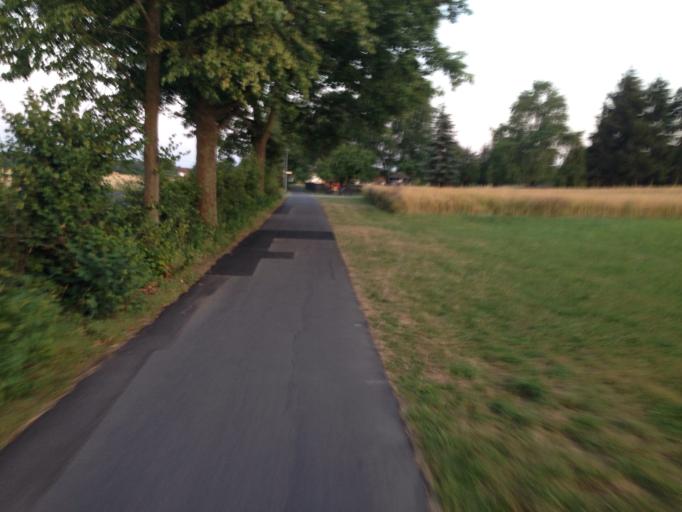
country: DE
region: Hesse
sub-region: Regierungsbezirk Giessen
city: Grossen Buseck
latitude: 50.5596
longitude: 8.7751
